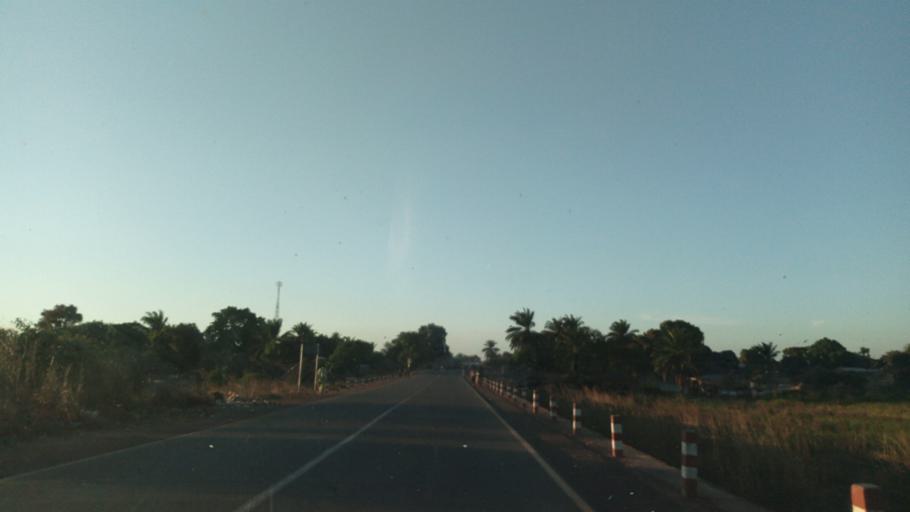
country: ZM
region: Luapula
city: Mwense
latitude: -10.7594
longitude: 28.2836
